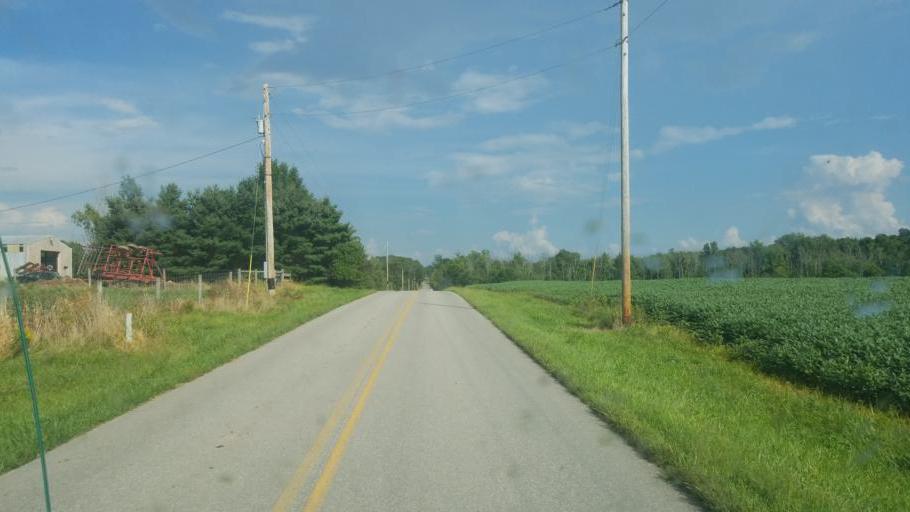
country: US
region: Ohio
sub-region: Huron County
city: Plymouth
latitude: 41.0070
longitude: -82.6303
